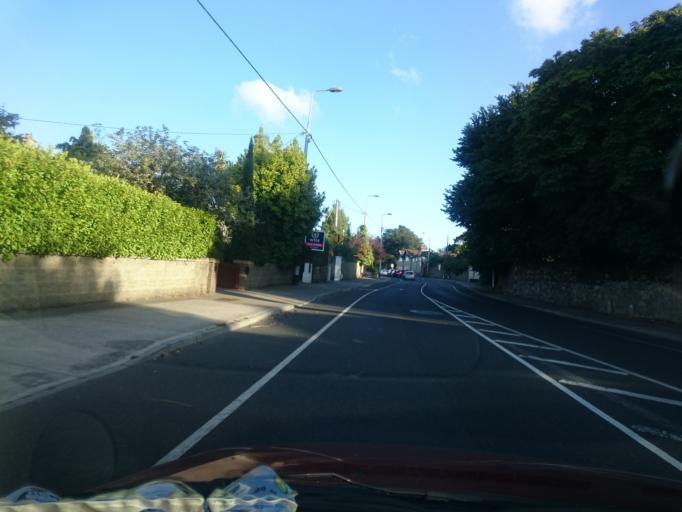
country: IE
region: Leinster
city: Balally
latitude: 53.2788
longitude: -6.2315
